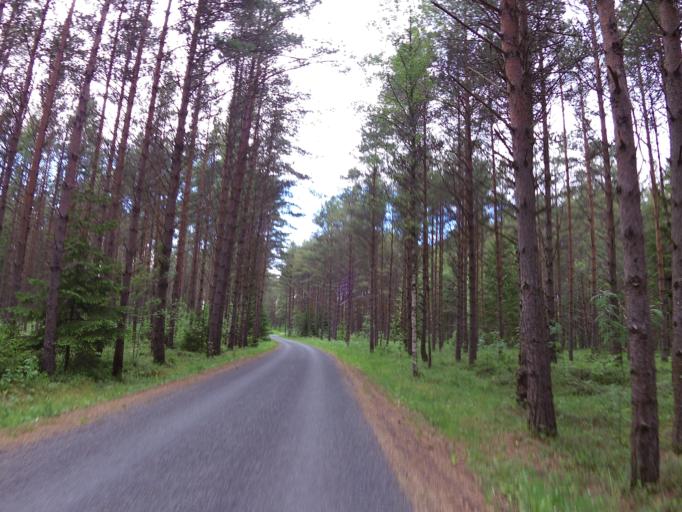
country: EE
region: Harju
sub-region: Paldiski linn
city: Paldiski
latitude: 59.2517
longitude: 23.7628
